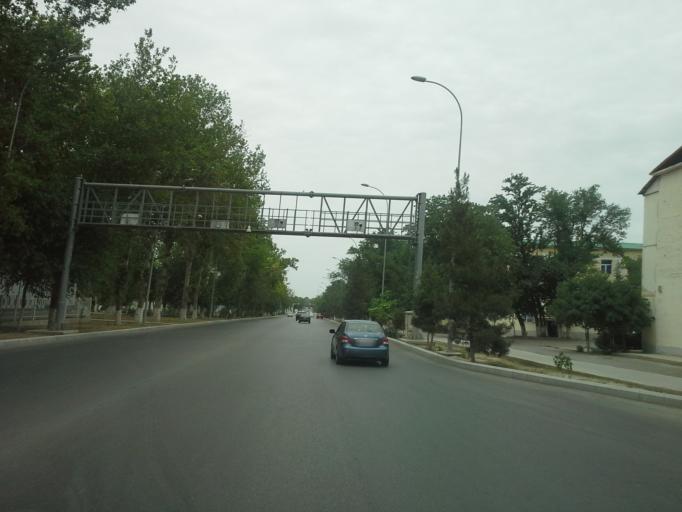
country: TM
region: Ahal
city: Ashgabat
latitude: 37.9142
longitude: 58.4061
